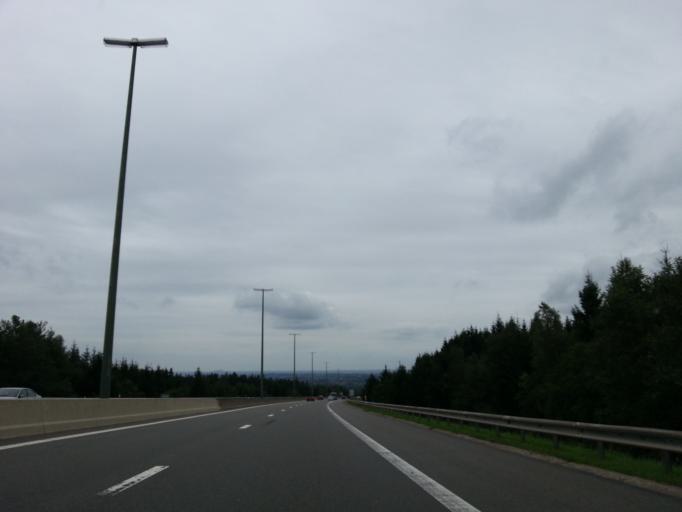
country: BE
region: Wallonia
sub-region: Province de Liege
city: Jalhay
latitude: 50.4828
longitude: 5.9551
